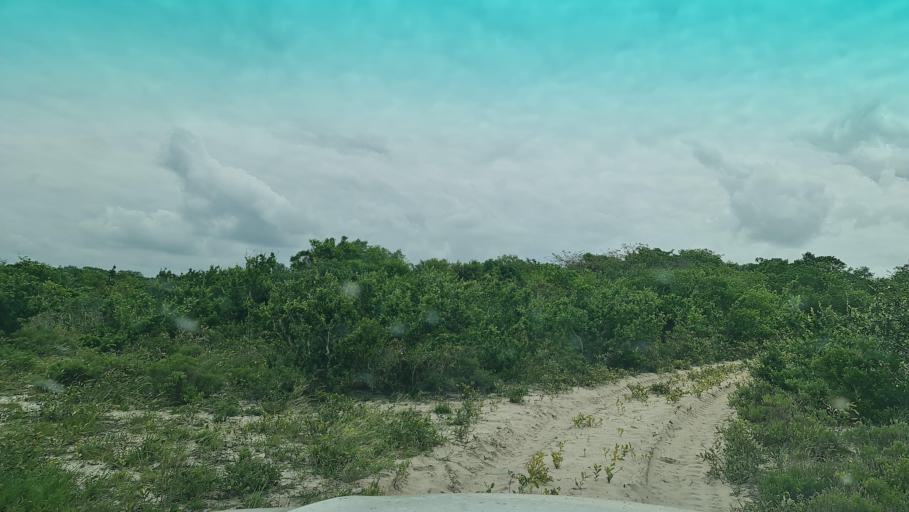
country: MZ
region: Maputo
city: Manhica
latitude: -25.6240
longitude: 32.7746
